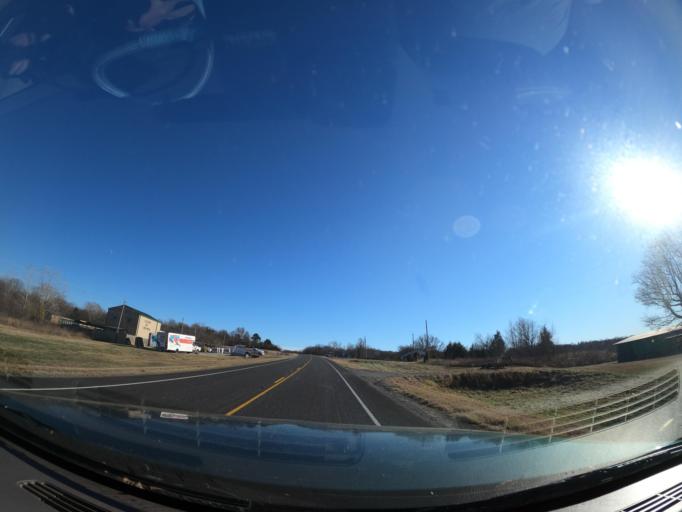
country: US
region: Oklahoma
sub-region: McIntosh County
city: Eufaula
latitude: 35.2560
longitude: -95.5771
